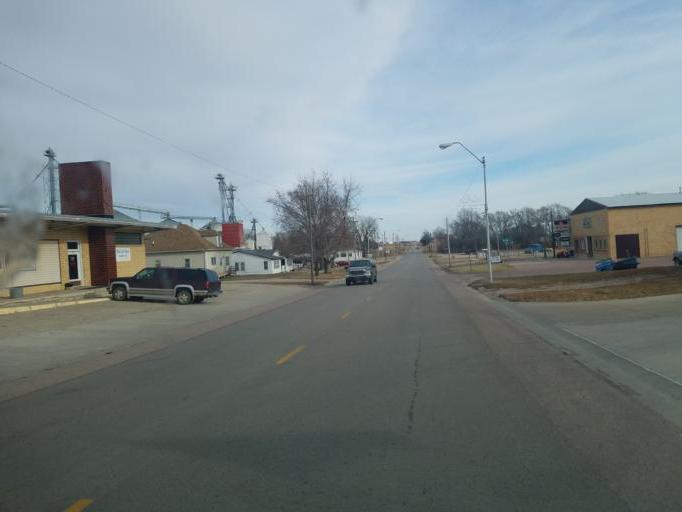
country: US
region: Nebraska
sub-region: Knox County
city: Creighton
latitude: 42.4667
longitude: -97.9025
